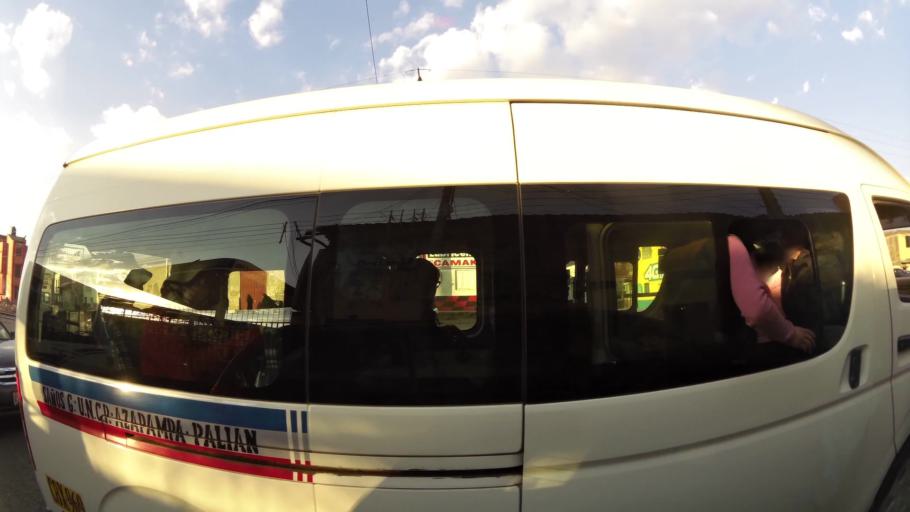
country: PE
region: Junin
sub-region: Provincia de Huancayo
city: El Tambo
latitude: -12.0541
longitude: -75.2136
